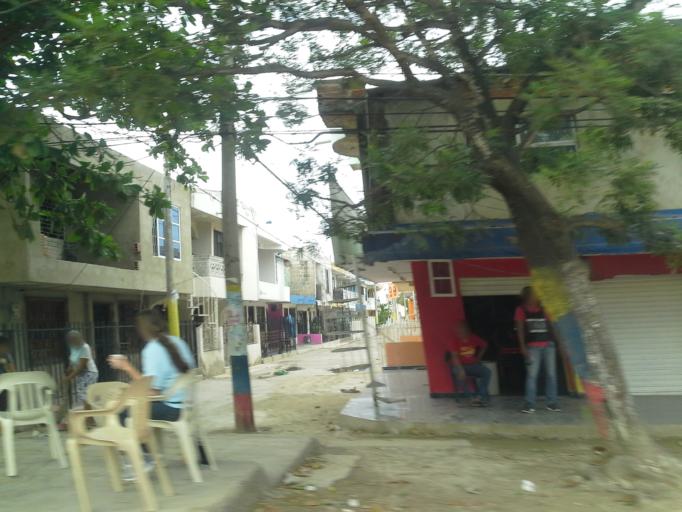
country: CO
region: Bolivar
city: Cartagena
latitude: 10.4007
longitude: -75.4702
